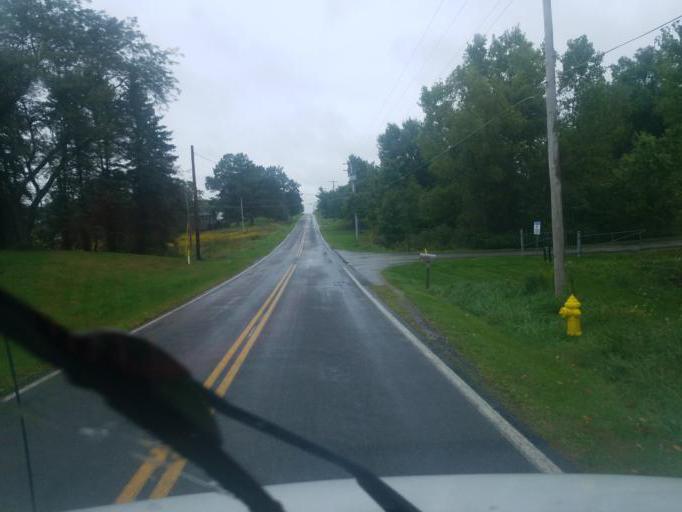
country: US
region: Ohio
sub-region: Wayne County
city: Rittman
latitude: 40.9958
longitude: -81.8154
